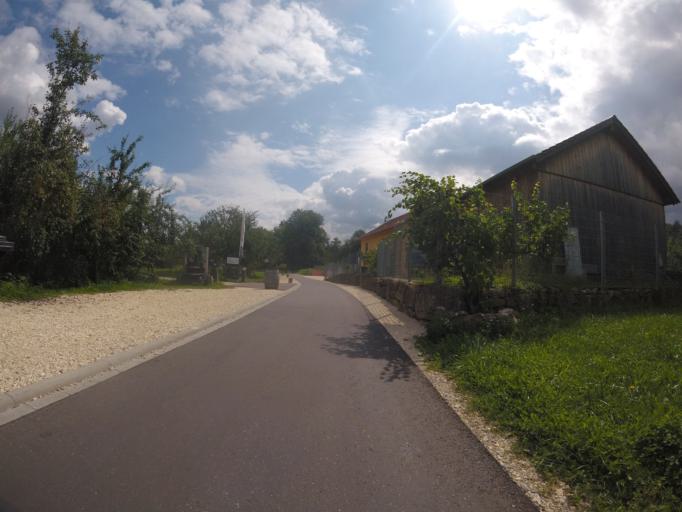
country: DE
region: Baden-Wuerttemberg
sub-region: Regierungsbezirk Stuttgart
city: Winterbach
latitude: 48.8075
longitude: 9.4364
